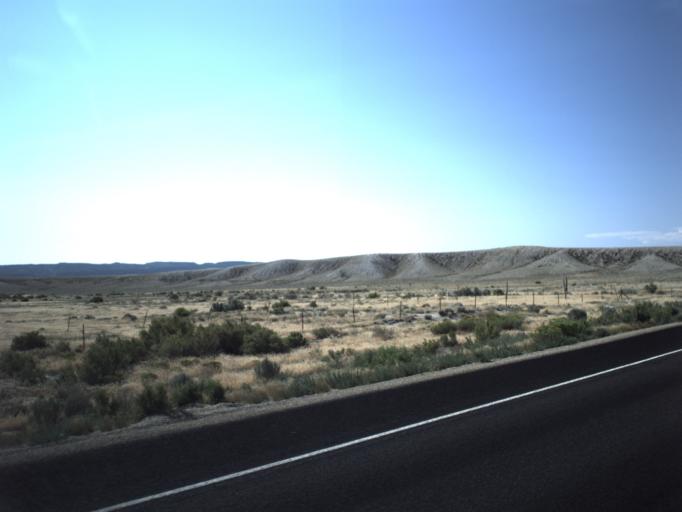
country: US
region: Utah
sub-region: Emery County
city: Ferron
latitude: 38.9839
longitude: -111.1723
